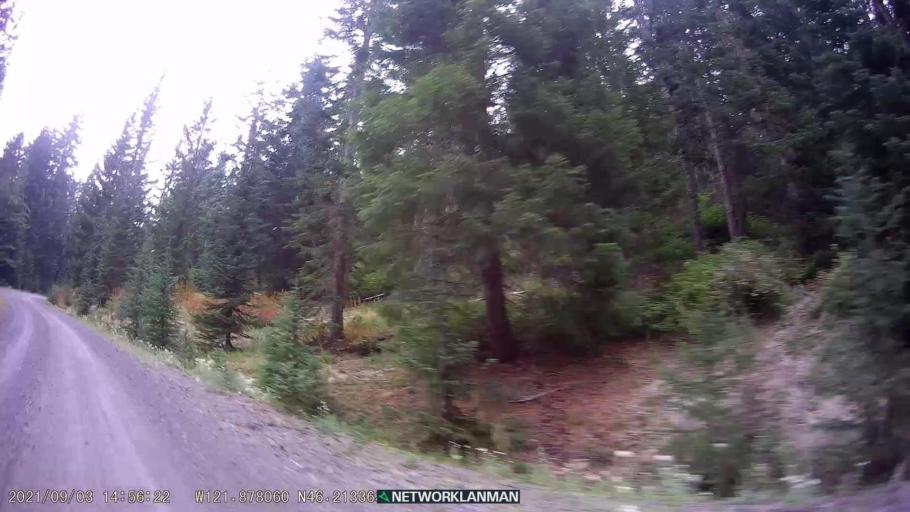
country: US
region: Washington
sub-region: Skamania County
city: Carson
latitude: 46.2135
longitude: -121.8783
